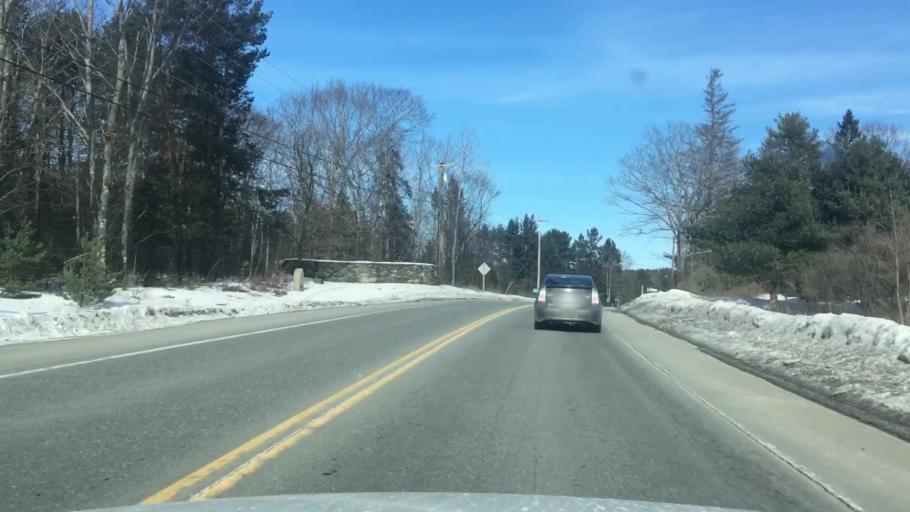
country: US
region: Maine
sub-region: Penobscot County
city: Orrington
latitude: 44.7379
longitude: -68.8201
